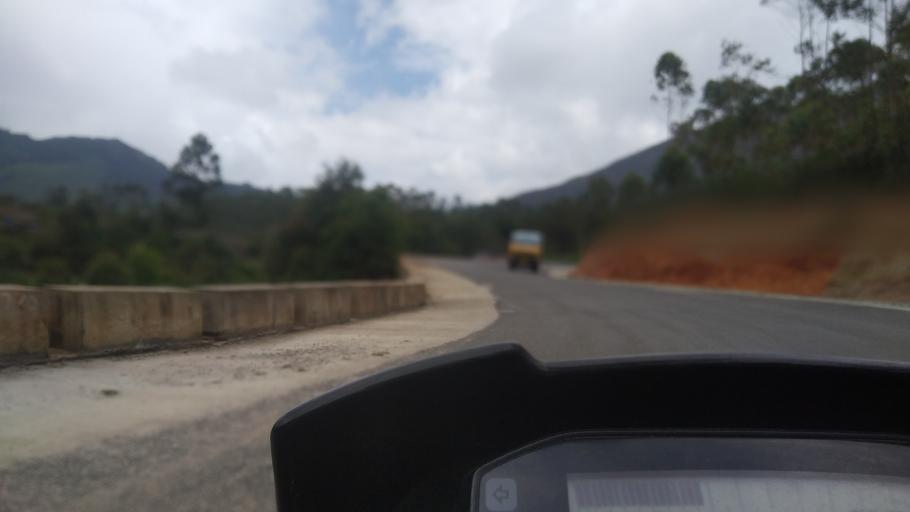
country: IN
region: Kerala
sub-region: Idukki
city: Munnar
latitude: 10.0504
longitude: 77.1111
